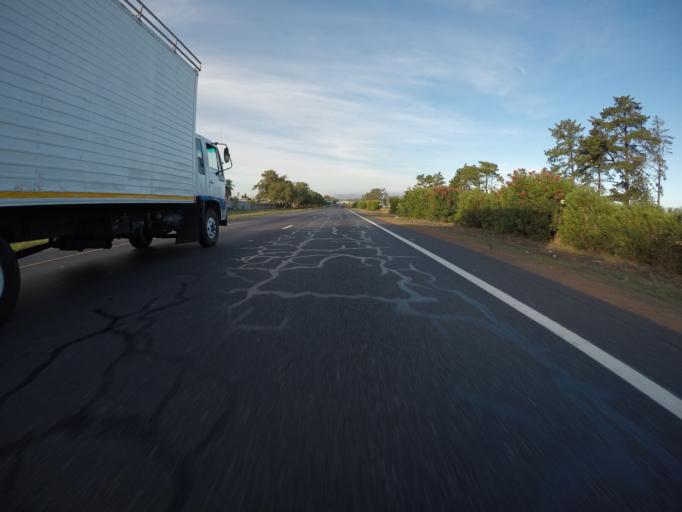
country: ZA
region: Western Cape
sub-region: City of Cape Town
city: Kraaifontein
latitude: -33.8539
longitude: 18.7017
